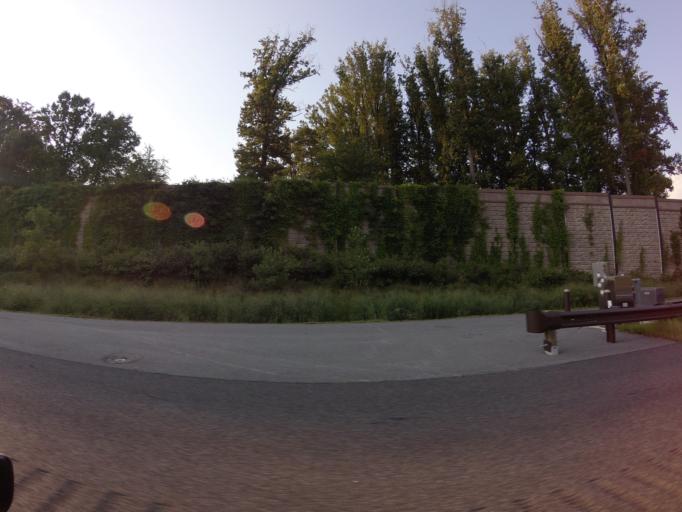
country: US
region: Maryland
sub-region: Montgomery County
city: Fairland
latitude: 39.0833
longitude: -76.9662
